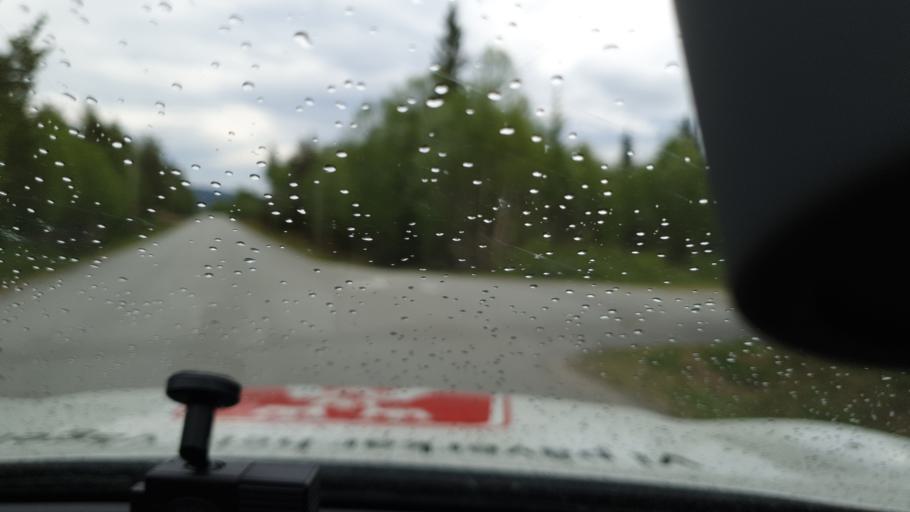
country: SE
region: Vaesterbotten
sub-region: Storumans Kommun
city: Fristad
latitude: 65.9572
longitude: 16.1942
